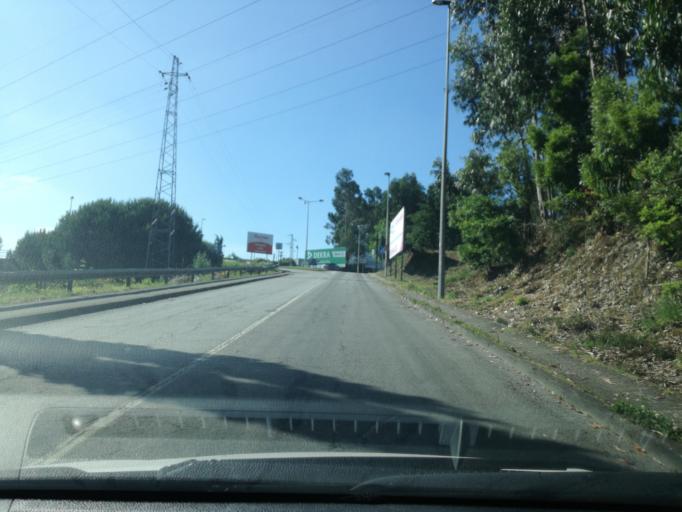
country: PT
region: Porto
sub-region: Maia
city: Maia
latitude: 41.2479
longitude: -8.6233
